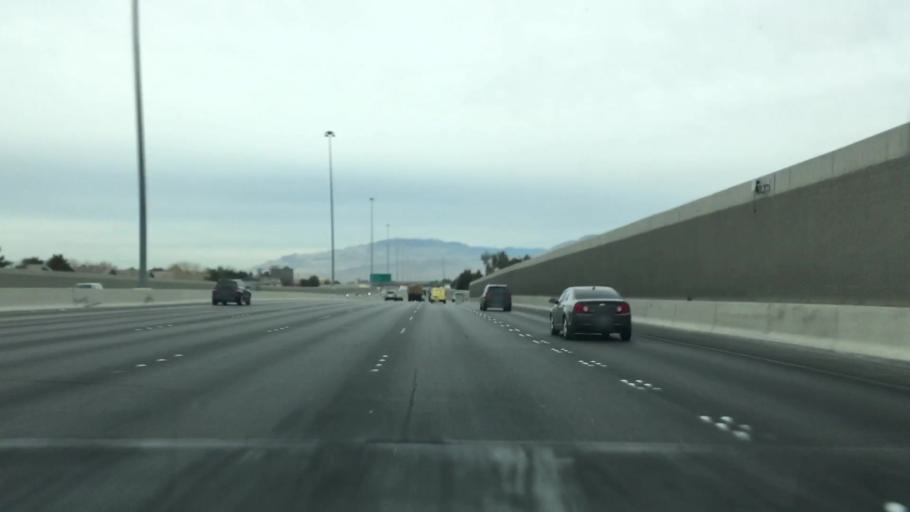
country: US
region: Nevada
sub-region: Clark County
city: Spring Valley
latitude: 36.2259
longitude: -115.2467
